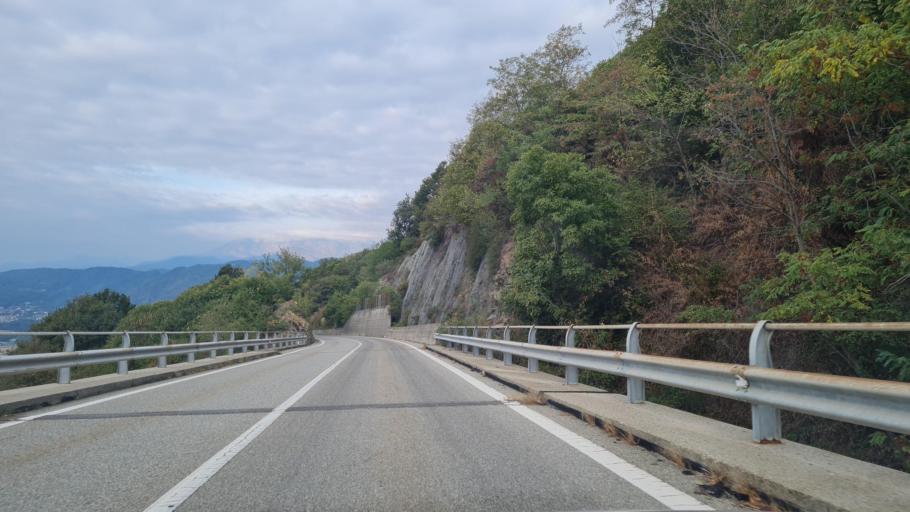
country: IT
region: Piedmont
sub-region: Provincia di Torino
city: Andrate
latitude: 45.5157
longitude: 7.8947
